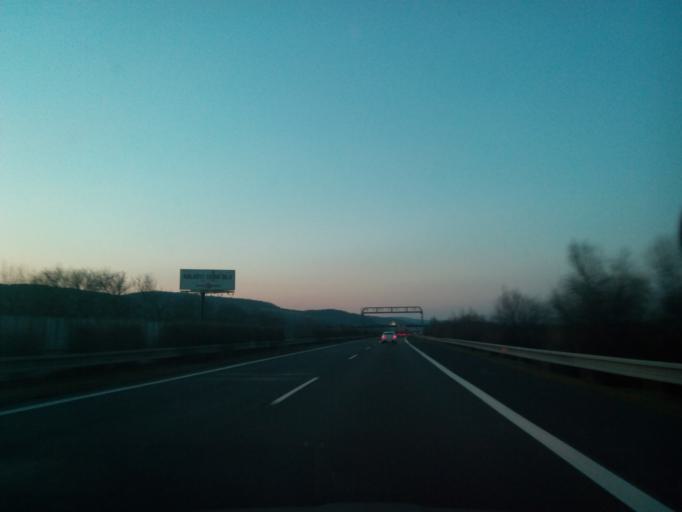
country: SK
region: Presovsky
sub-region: Okres Presov
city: Presov
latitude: 48.8746
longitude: 21.2534
